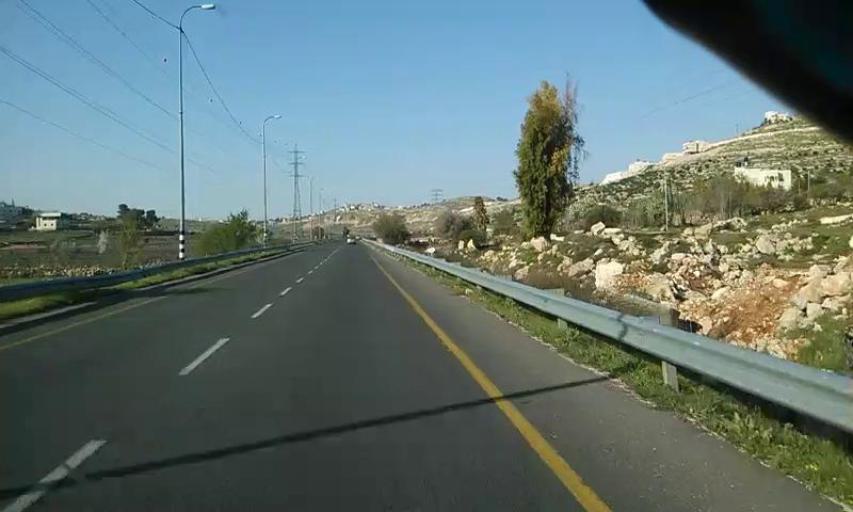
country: PS
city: Al Buq`ah
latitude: 31.5468
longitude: 35.1338
